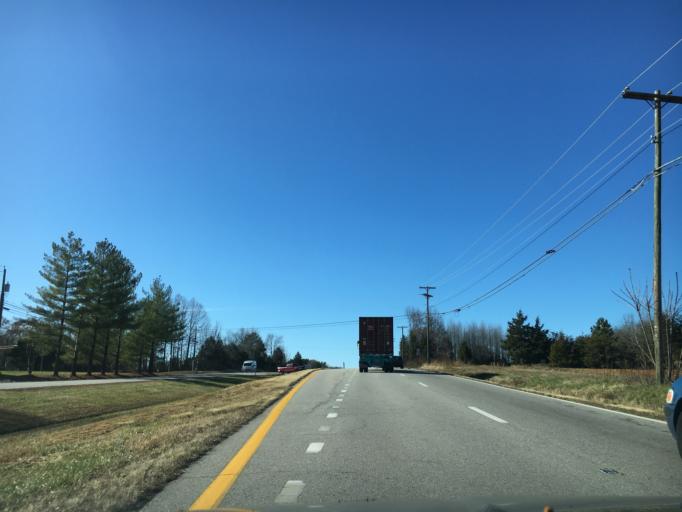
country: US
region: Virginia
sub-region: Pittsylvania County
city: Mount Hermon
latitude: 36.6093
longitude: -79.5542
